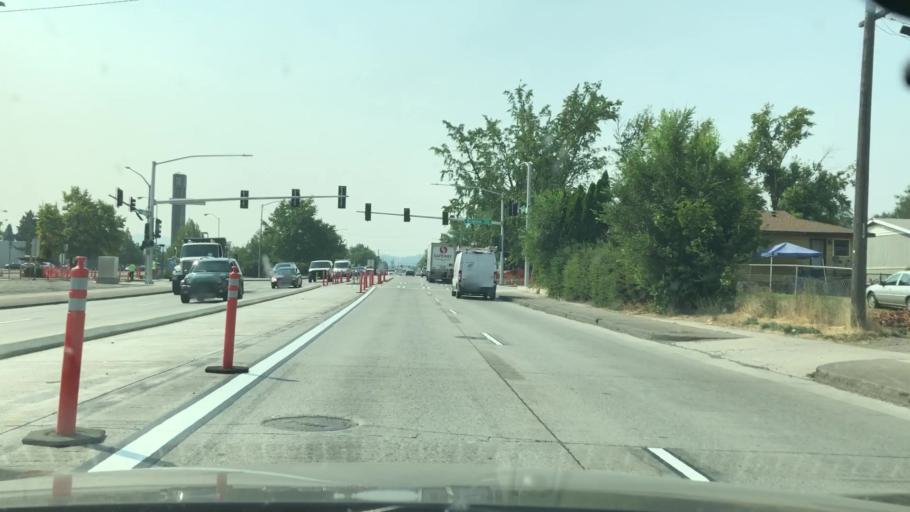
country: US
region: Washington
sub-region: Spokane County
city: Spokane
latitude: 47.6771
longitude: -117.3638
